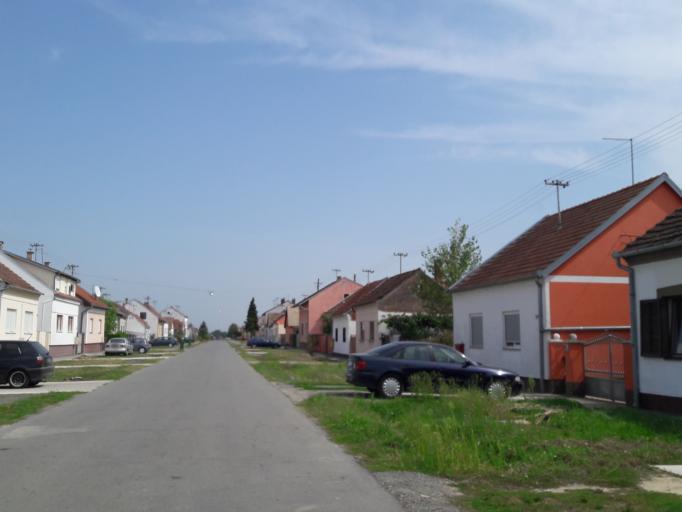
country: HR
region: Osjecko-Baranjska
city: Cepin
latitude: 45.5264
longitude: 18.5650
